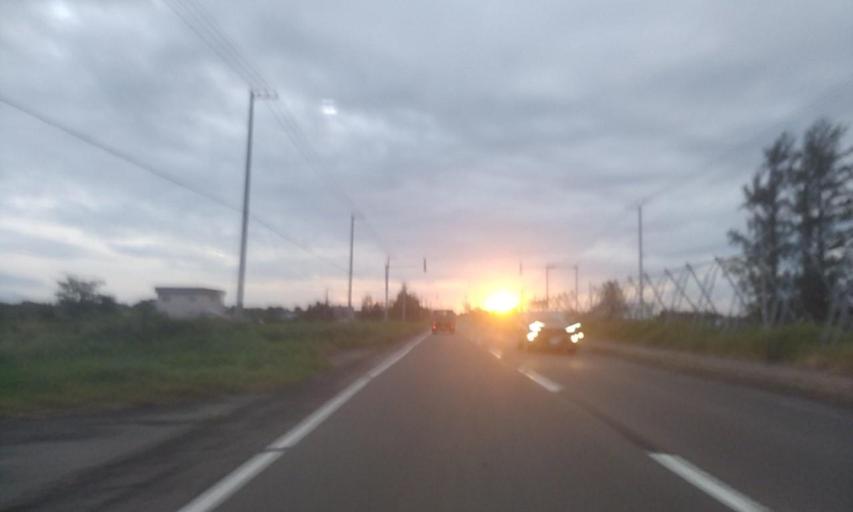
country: JP
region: Hokkaido
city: Abashiri
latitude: 43.9002
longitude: 144.6481
